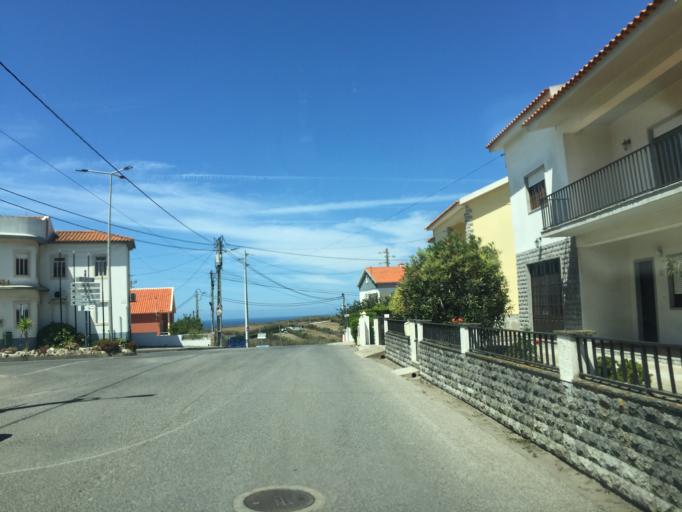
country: PT
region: Lisbon
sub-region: Lourinha
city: Lourinha
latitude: 39.2044
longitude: -9.3345
